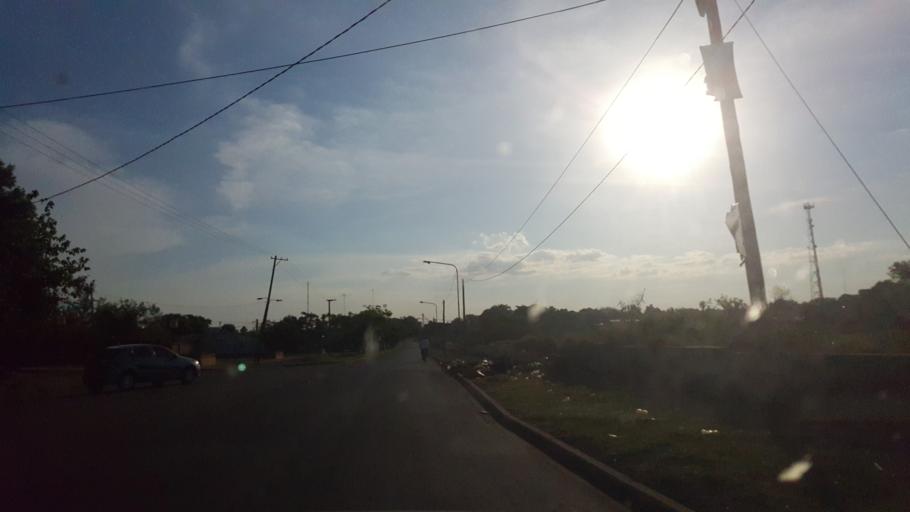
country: AR
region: Misiones
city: Garupa
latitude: -27.4351
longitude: -55.8787
